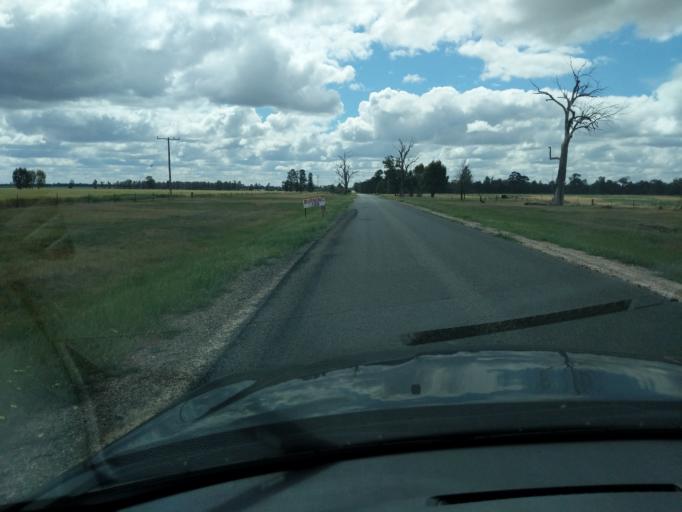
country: AU
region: New South Wales
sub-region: Coolamon
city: Coolamon
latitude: -34.8587
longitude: 146.8983
